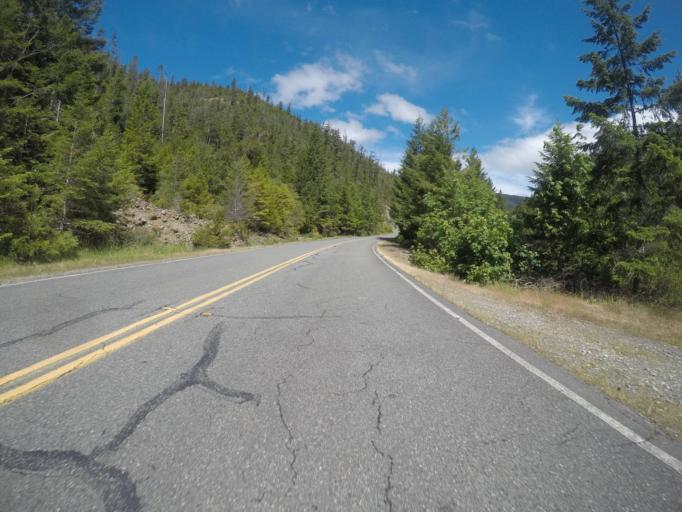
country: US
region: California
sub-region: Del Norte County
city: Bertsch-Oceanview
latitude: 41.7051
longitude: -123.9392
